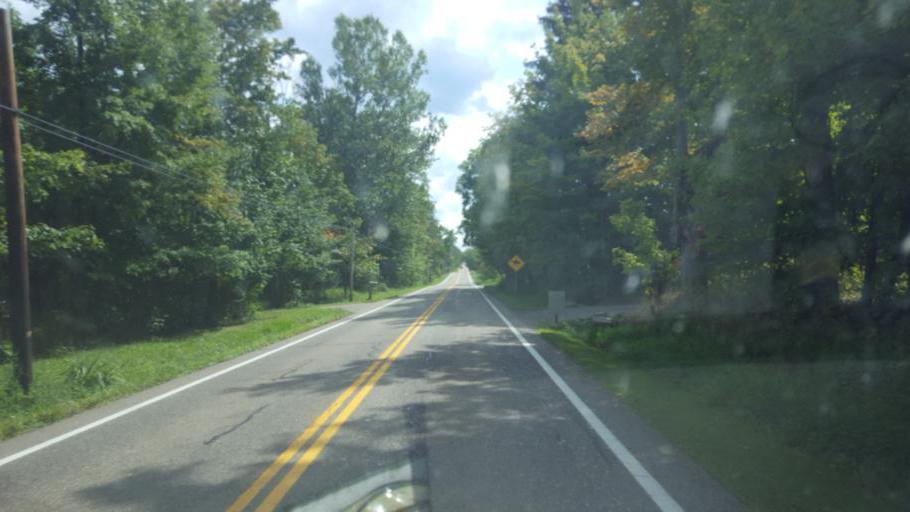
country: US
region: Ohio
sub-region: Portage County
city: Hiram
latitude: 41.3360
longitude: -81.1433
